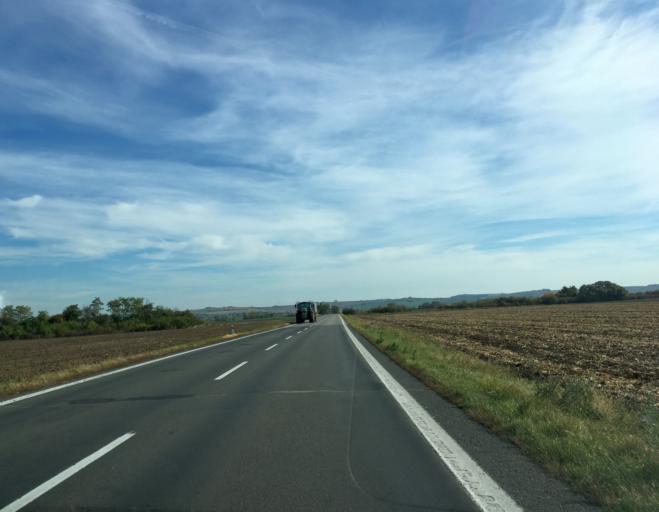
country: SK
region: Nitriansky
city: Zeliezovce
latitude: 48.1235
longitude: 18.6637
